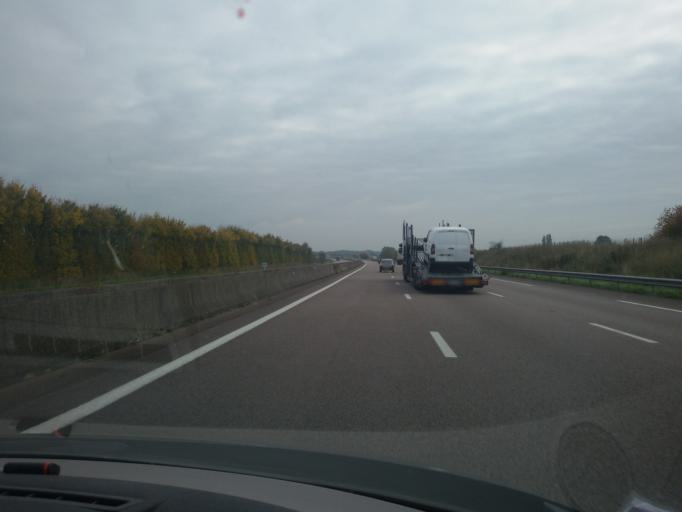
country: FR
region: Haute-Normandie
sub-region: Departement de l'Eure
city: Vernon
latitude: 49.0416
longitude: 1.4531
